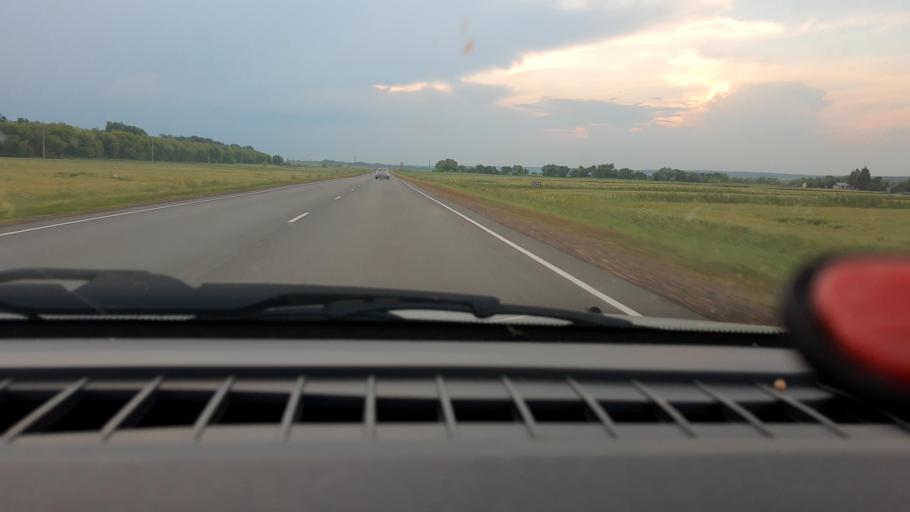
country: RU
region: Nizjnij Novgorod
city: Shatki
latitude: 55.2631
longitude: 43.9732
